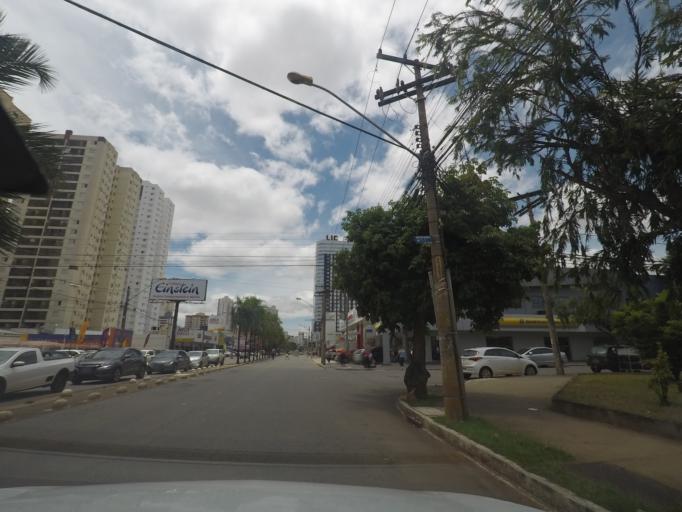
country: BR
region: Goias
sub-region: Goiania
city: Goiania
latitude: -16.6915
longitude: -49.2774
